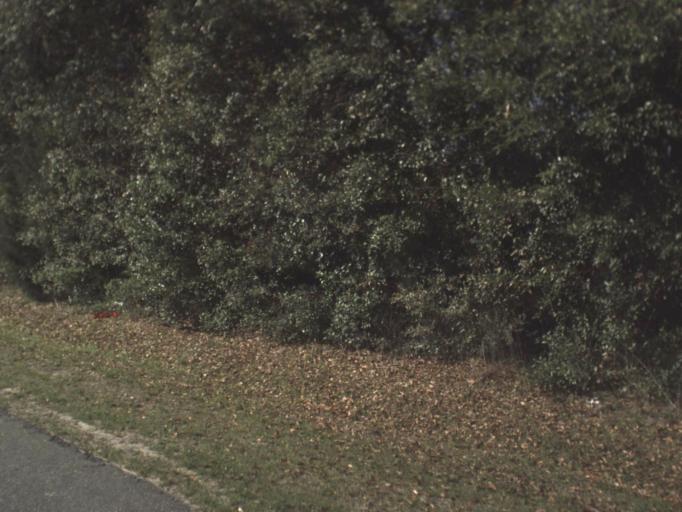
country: US
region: Florida
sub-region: Jackson County
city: Malone
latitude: 30.8942
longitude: -85.1612
